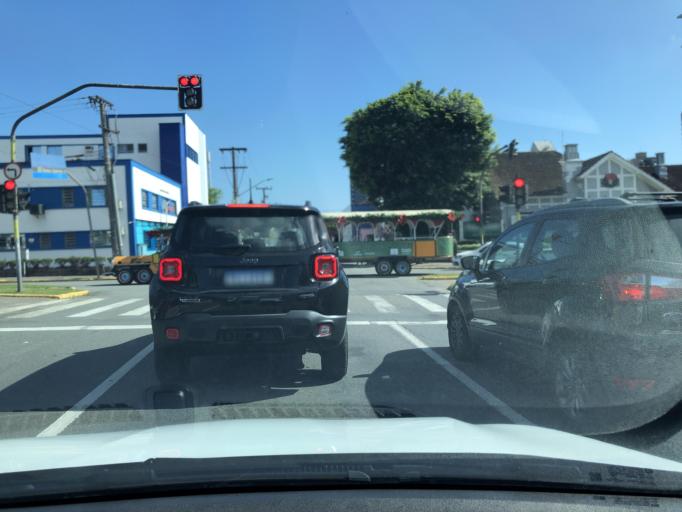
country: BR
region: Santa Catarina
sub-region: Joinville
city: Joinville
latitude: -26.3014
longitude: -48.8421
